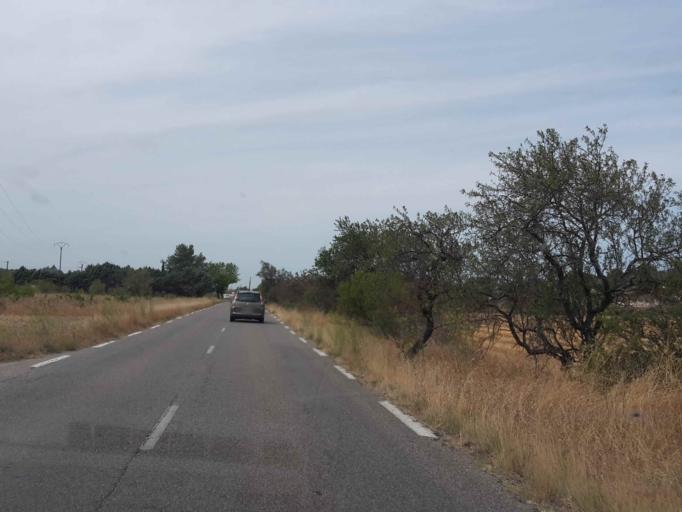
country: FR
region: Provence-Alpes-Cote d'Azur
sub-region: Departement des Bouches-du-Rhone
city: Lancon-Provence
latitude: 43.5866
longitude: 5.1585
